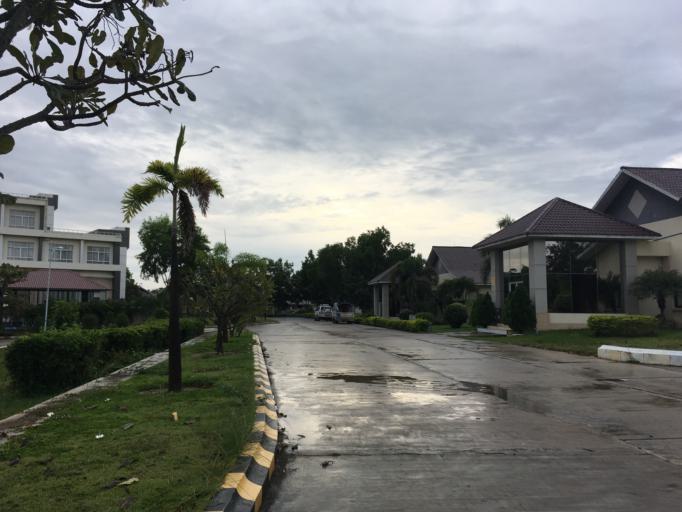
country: MM
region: Mandalay
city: Nay Pyi Taw
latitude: 19.7016
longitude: 96.1177
